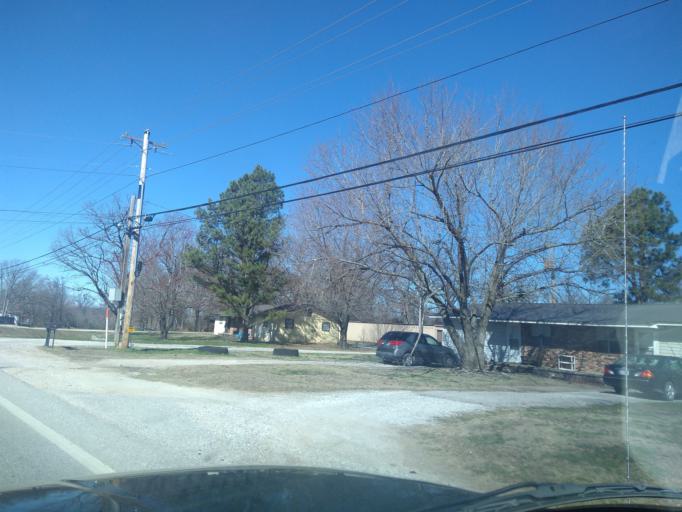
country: US
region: Arkansas
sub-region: Washington County
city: Farmington
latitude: 36.0793
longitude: -94.2599
